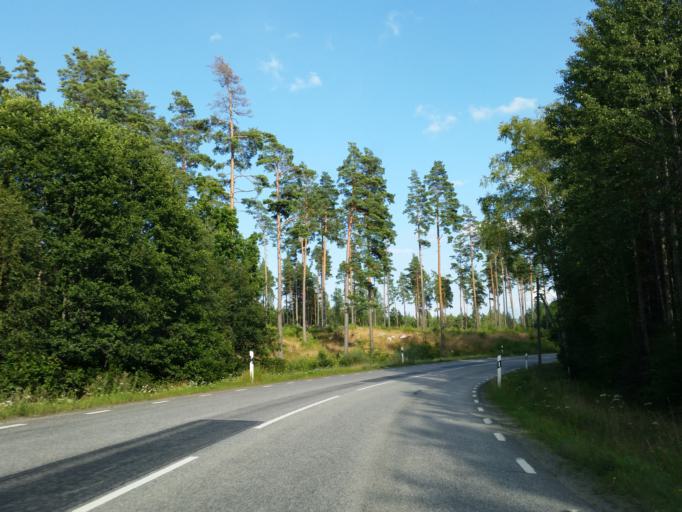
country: SE
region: Stockholm
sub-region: Nykvarns Kommun
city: Nykvarn
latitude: 59.2079
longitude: 17.3792
